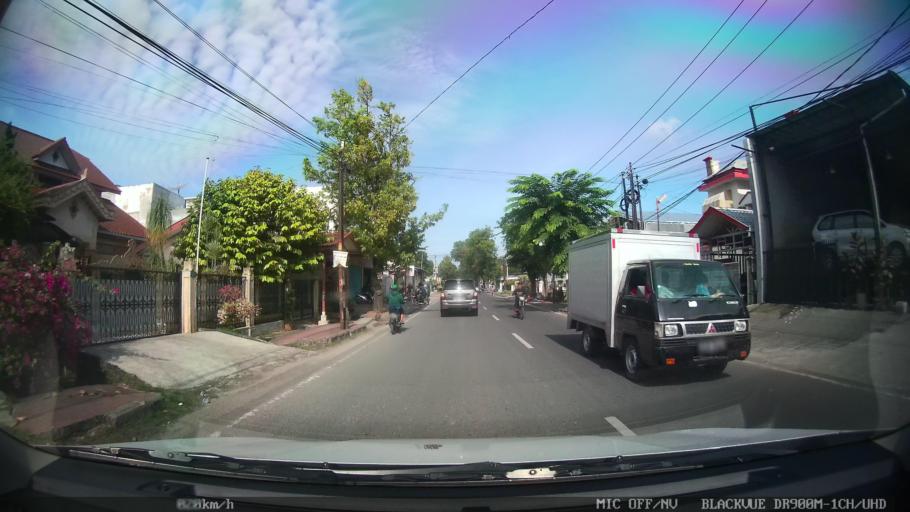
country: ID
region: North Sumatra
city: Medan
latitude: 3.6045
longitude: 98.6501
